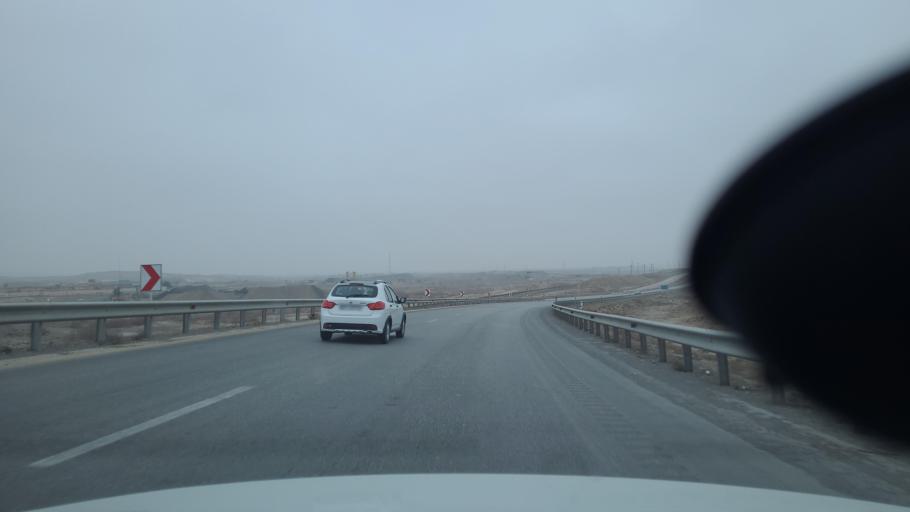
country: IR
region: Razavi Khorasan
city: Fariman
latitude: 35.9984
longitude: 59.7593
